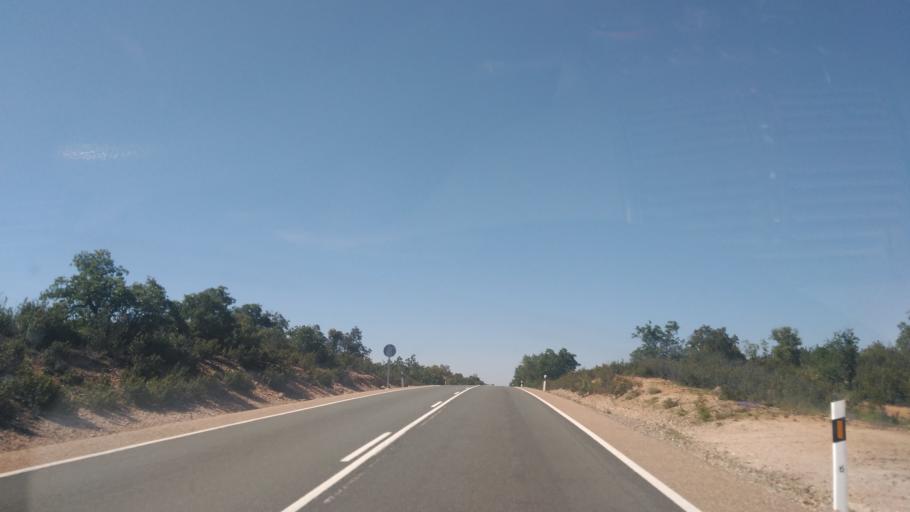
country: ES
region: Castille and Leon
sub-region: Provincia de Zamora
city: Corrales
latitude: 41.2923
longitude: -5.7239
